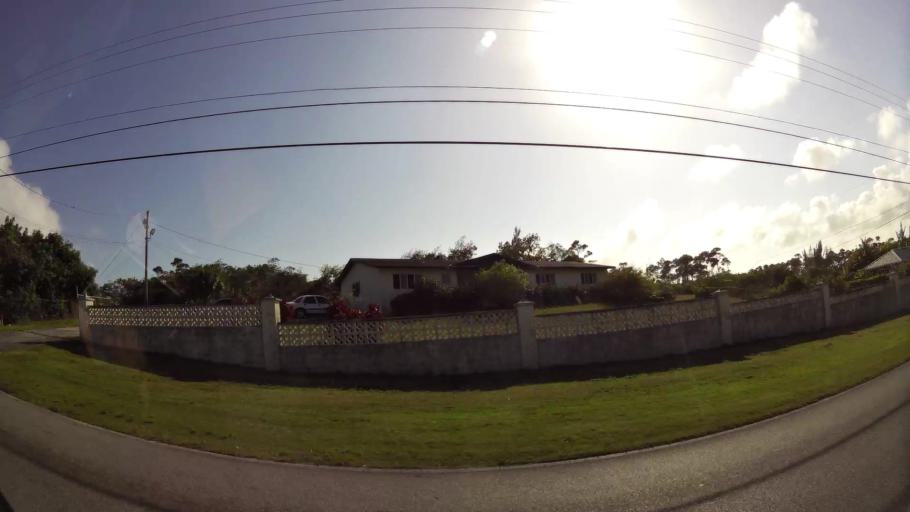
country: BS
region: Freeport
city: Lucaya
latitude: 26.5148
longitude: -78.6648
